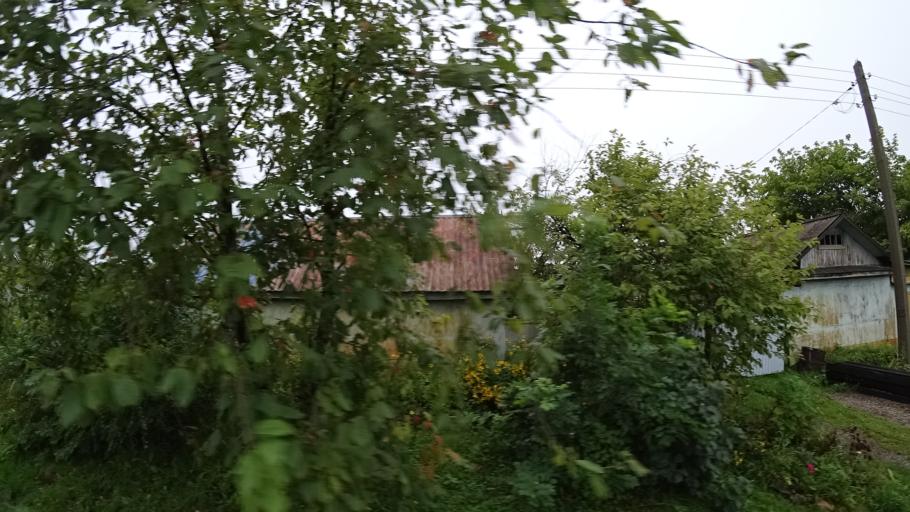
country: RU
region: Primorskiy
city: Monastyrishche
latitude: 44.2082
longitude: 132.4517
